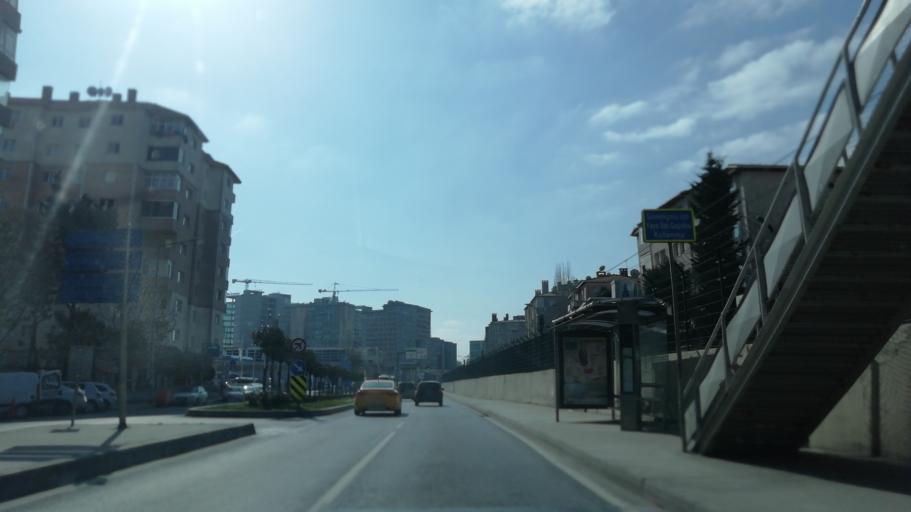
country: TR
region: Istanbul
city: merter keresteciler
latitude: 41.0155
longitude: 28.9003
